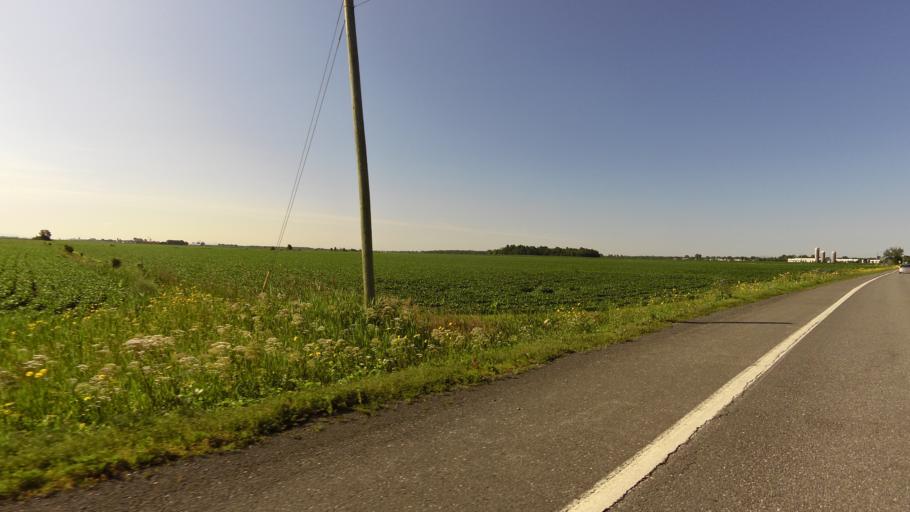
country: CA
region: Quebec
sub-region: Monteregie
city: Napierville
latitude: 45.2446
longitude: -73.3917
